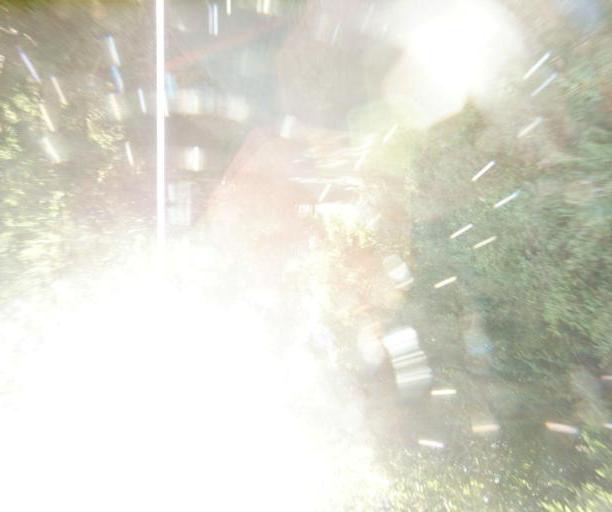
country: FR
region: Rhone-Alpes
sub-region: Departement du Rhone
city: Saint-Pierre-la-Palud
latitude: 45.7718
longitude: 4.6028
